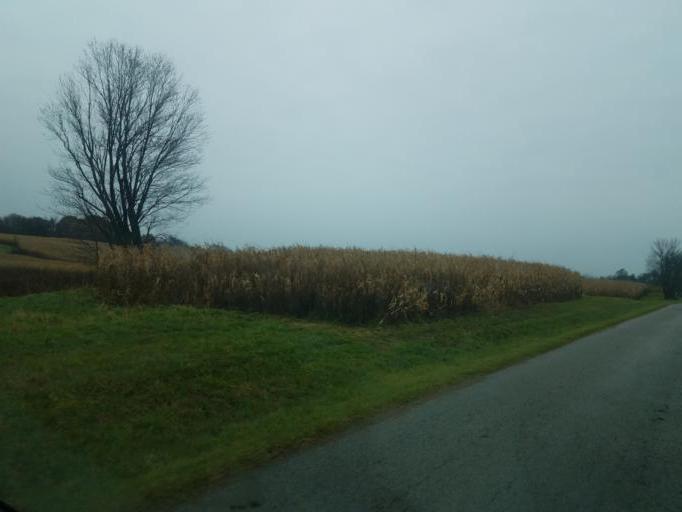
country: US
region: Ohio
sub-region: Knox County
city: Centerburg
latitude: 40.3632
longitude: -82.7072
